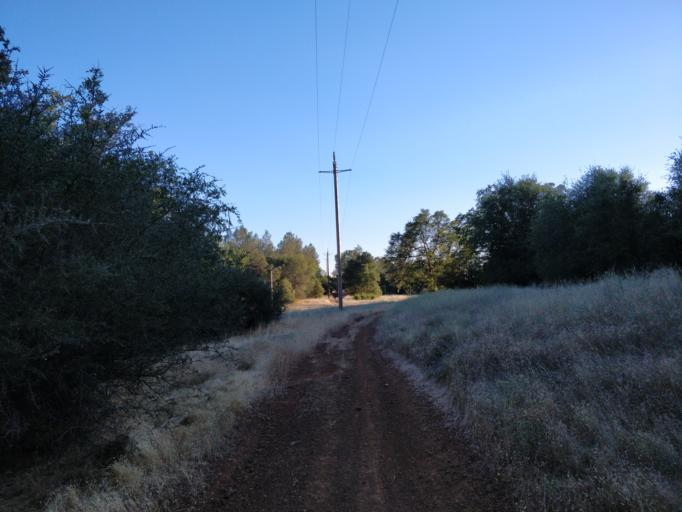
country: US
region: California
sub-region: Shasta County
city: Shasta Lake
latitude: 40.6666
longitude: -122.3669
